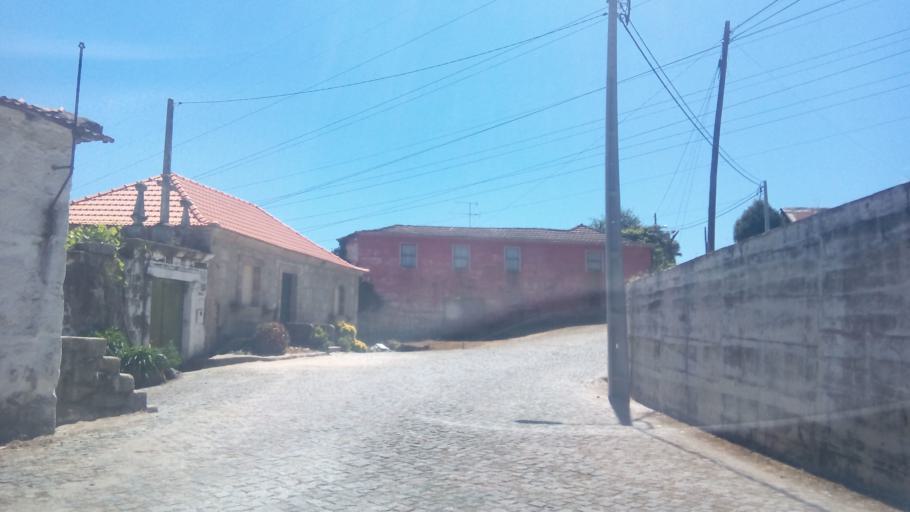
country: PT
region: Porto
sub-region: Paredes
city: Casteloes de Cepeda
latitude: 41.1907
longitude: -8.3407
